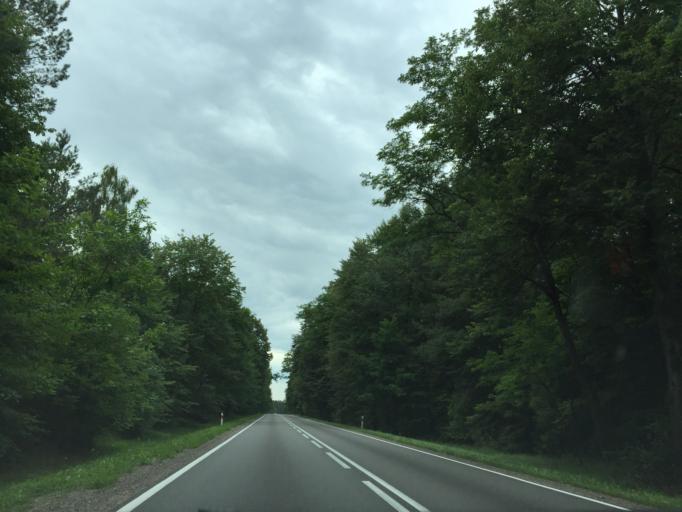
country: PL
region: Podlasie
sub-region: Powiat bialostocki
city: Zabludow
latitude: 52.9070
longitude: 23.2374
